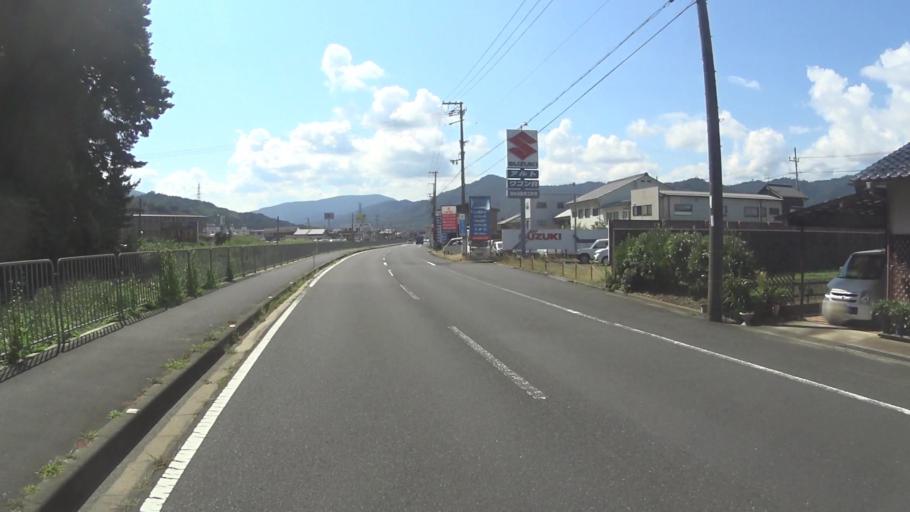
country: JP
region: Kyoto
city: Miyazu
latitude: 35.5398
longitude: 135.2076
